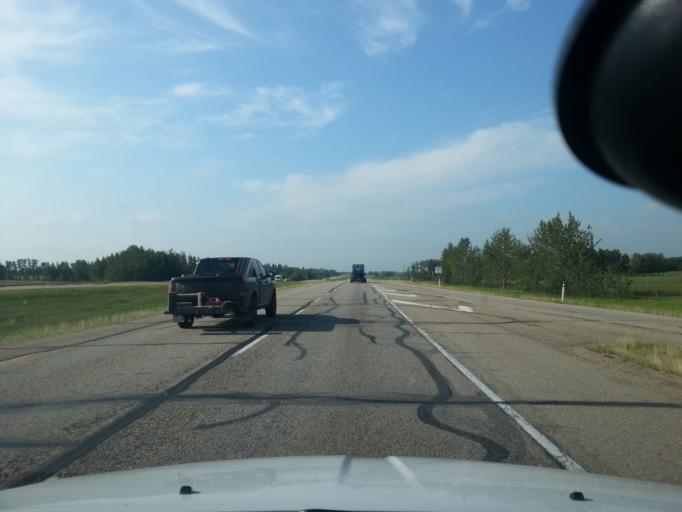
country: CA
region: Alberta
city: Lacombe
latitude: 52.5535
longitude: -113.6639
